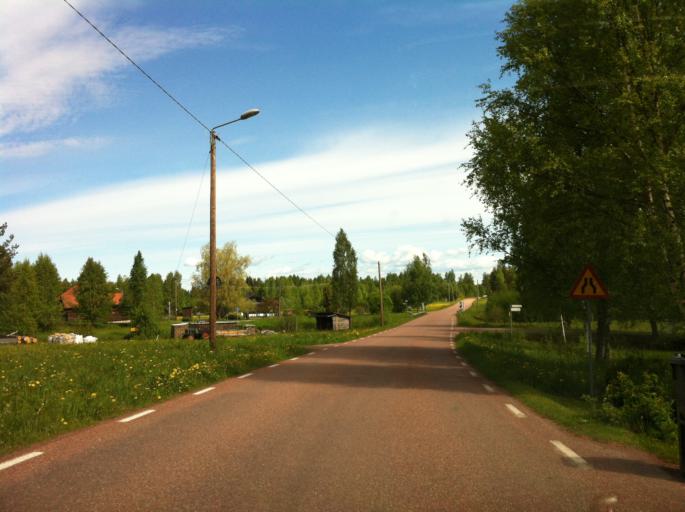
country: SE
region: Dalarna
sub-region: Mora Kommun
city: Mora
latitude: 60.8872
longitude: 14.5452
